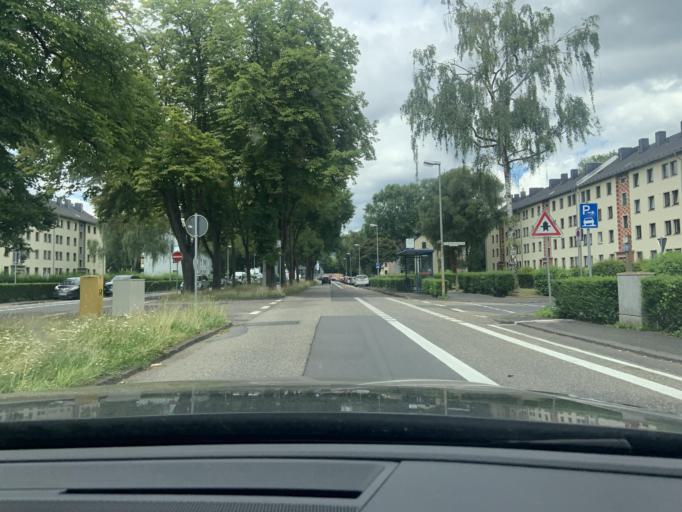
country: DE
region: Rheinland-Pfalz
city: Neuwied
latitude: 50.4350
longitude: 7.4546
